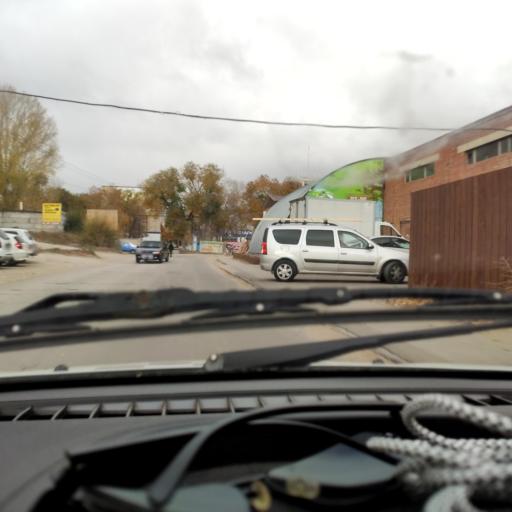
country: RU
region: Samara
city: Zhigulevsk
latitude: 53.4885
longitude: 49.4794
